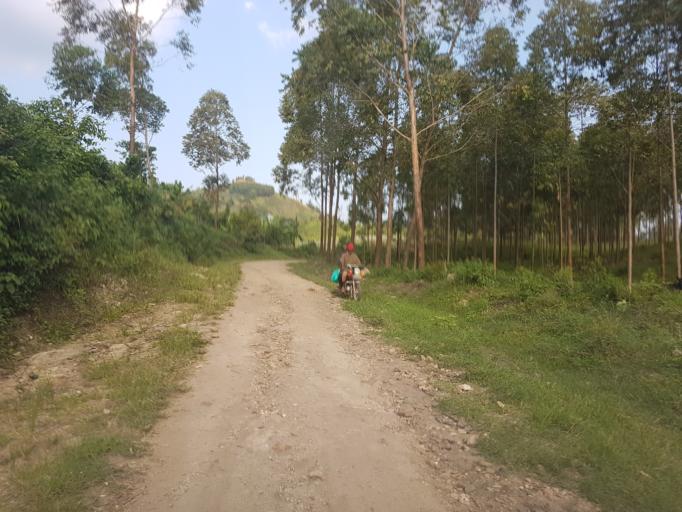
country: UG
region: Western Region
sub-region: Mitoma District
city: Mitoma
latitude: -0.6763
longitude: 29.9003
